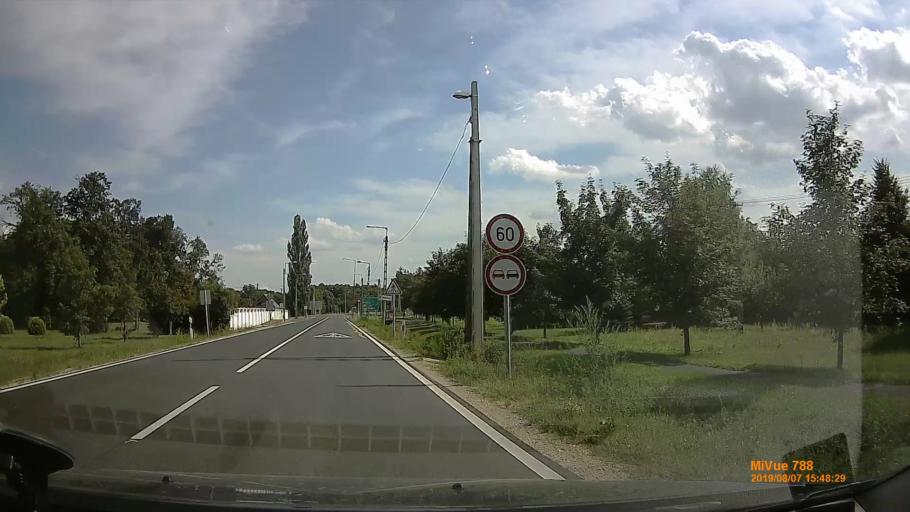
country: HU
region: Vas
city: Jak
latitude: 47.1609
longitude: 16.6375
